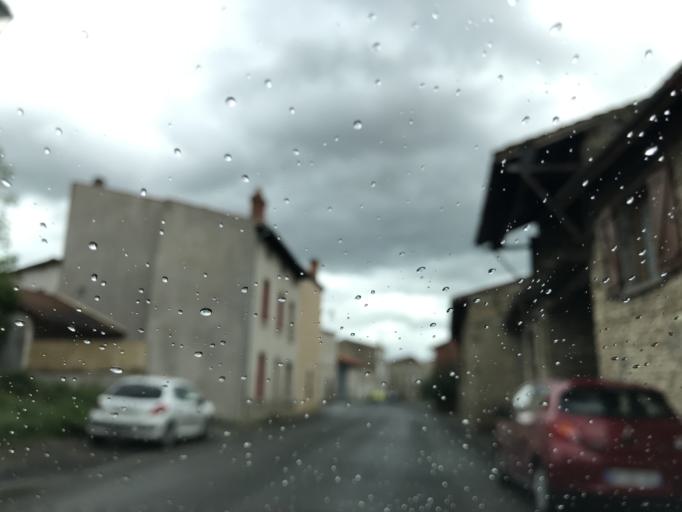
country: FR
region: Auvergne
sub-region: Departement du Puy-de-Dome
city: Billom
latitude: 45.7513
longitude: 3.3350
